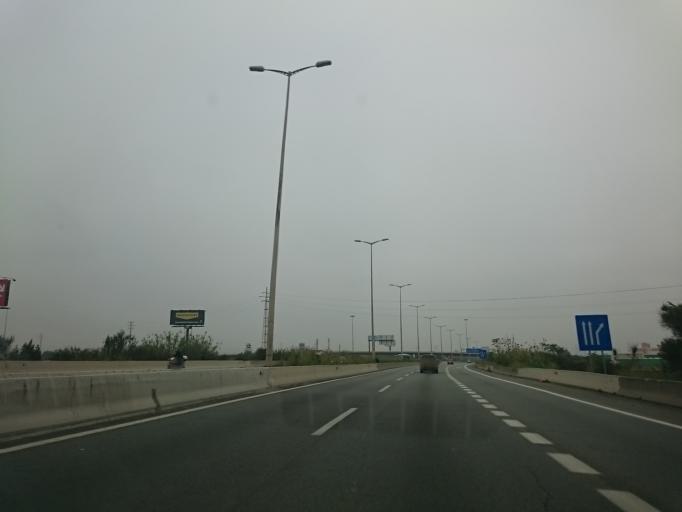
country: ES
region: Catalonia
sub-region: Provincia de Barcelona
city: El Prat de Llobregat
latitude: 41.3273
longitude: 2.0793
